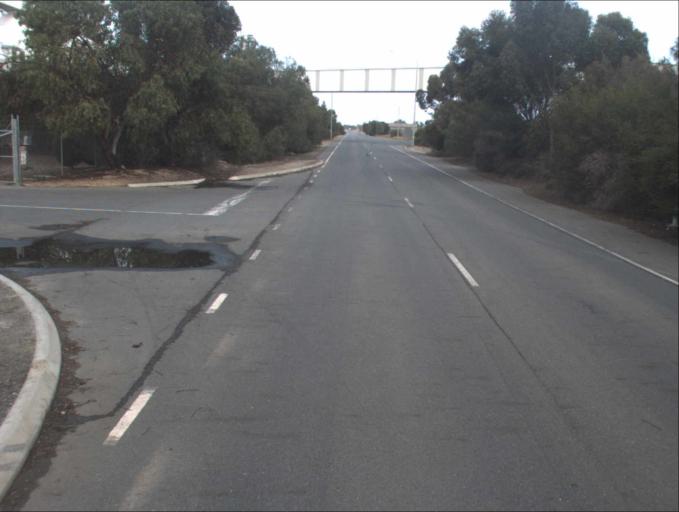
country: AU
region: South Australia
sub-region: Port Adelaide Enfield
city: Birkenhead
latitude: -34.7684
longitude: 138.5016
